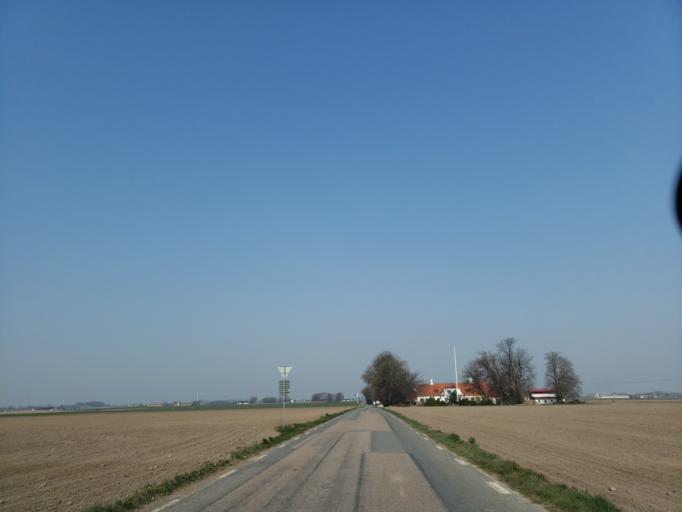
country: SE
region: Skane
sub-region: Simrishamns Kommun
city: Simrishamn
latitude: 55.4426
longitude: 14.2196
